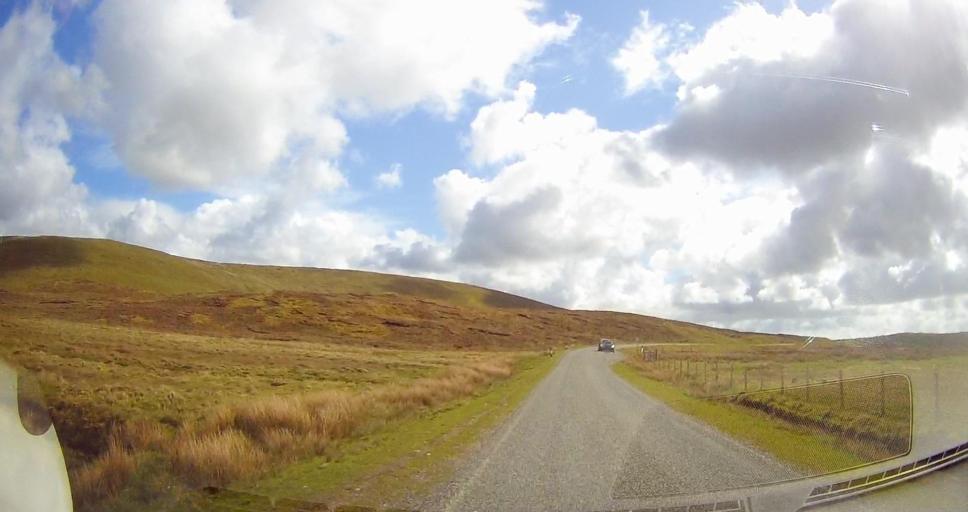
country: GB
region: Scotland
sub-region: Shetland Islands
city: Lerwick
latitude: 60.5178
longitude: -1.3778
